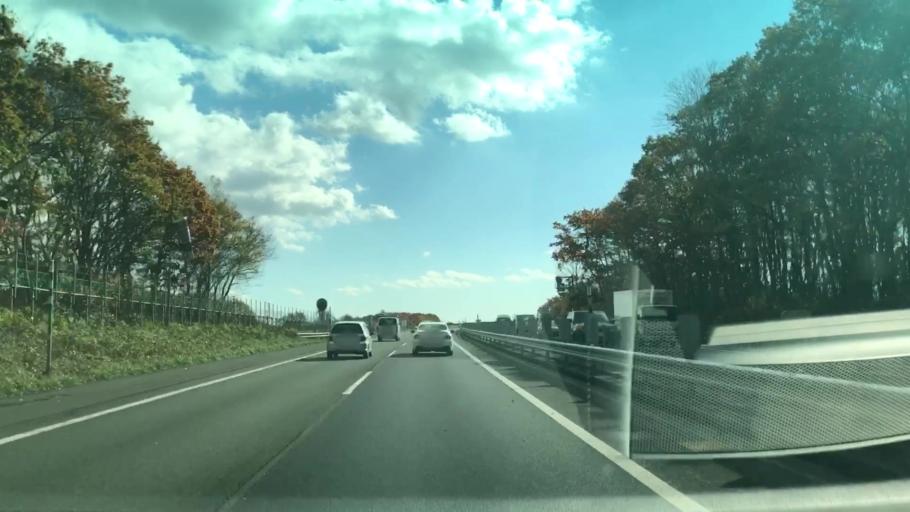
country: JP
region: Hokkaido
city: Kitahiroshima
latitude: 42.9176
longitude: 141.5466
